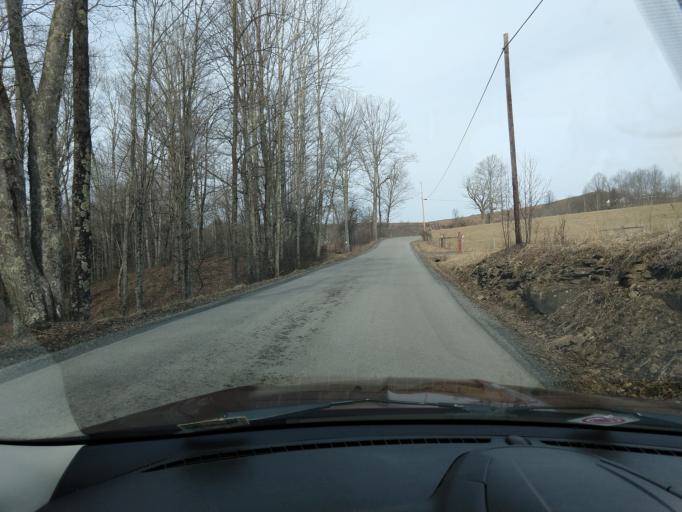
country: US
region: West Virginia
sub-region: Tucker County
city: Parsons
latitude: 39.0080
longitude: -79.5089
